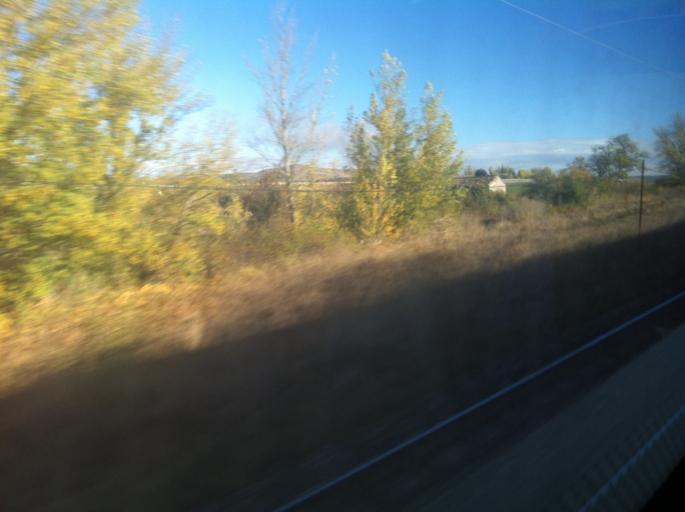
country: ES
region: Castille and Leon
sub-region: Provincia de Burgos
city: Villaldemiro
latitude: 42.2468
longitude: -3.9606
